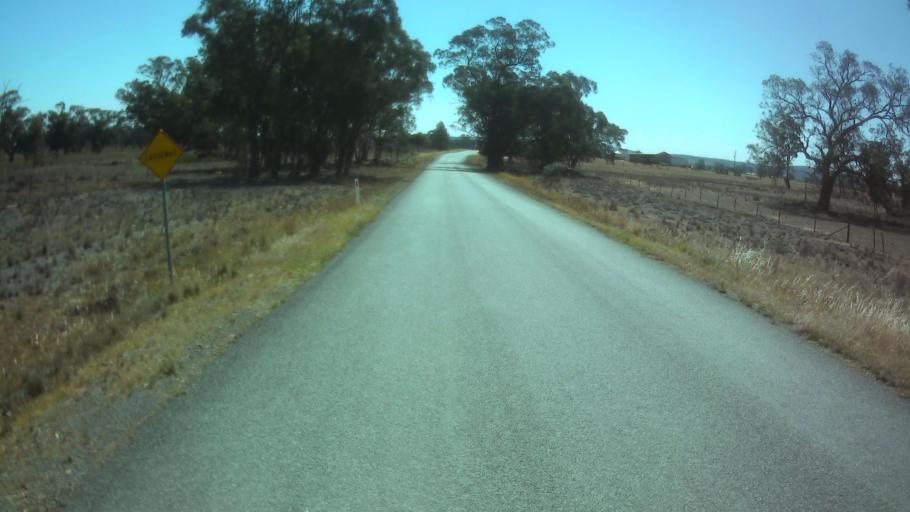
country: AU
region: New South Wales
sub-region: Weddin
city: Grenfell
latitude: -33.8164
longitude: 147.9431
